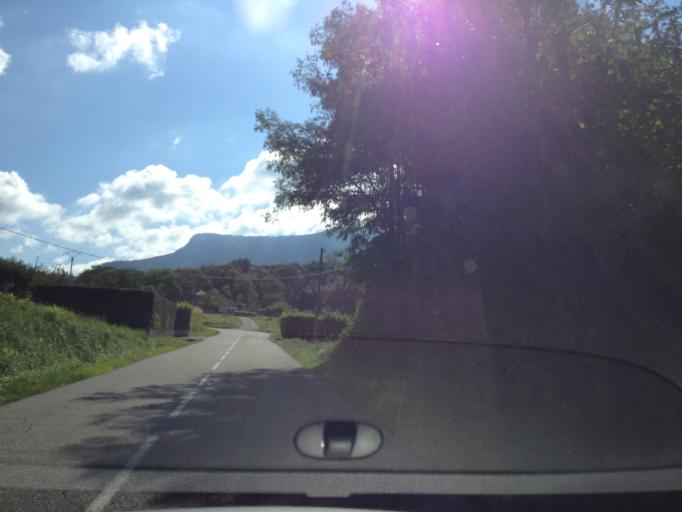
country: FR
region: Rhone-Alpes
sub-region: Departement de la Savoie
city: Gresy-sur-Aix
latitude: 45.7176
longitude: 5.9419
